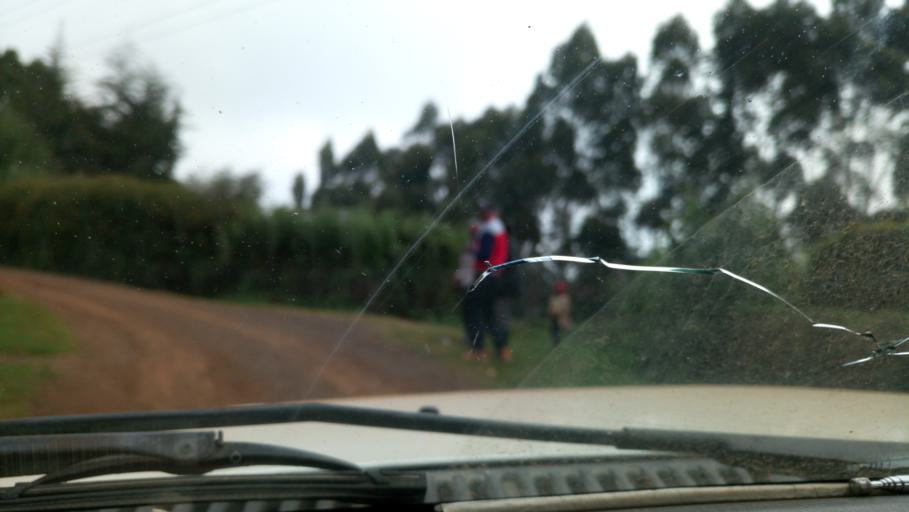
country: KE
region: Murang'a District
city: Kangema
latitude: -0.6407
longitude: 36.8316
